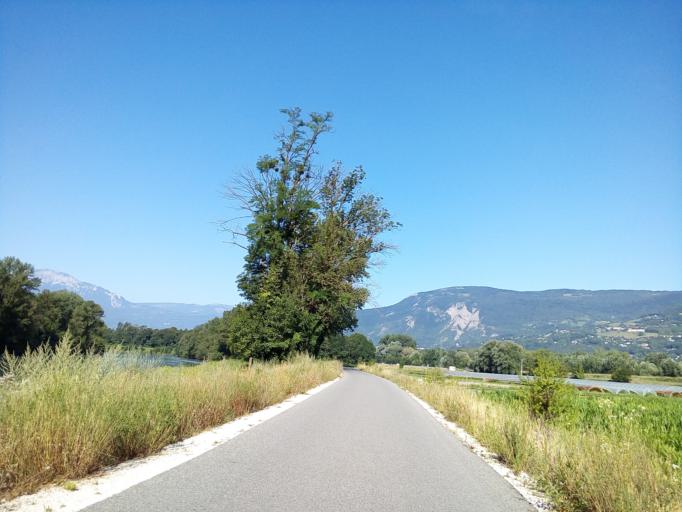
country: FR
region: Rhone-Alpes
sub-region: Departement de l'Isere
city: Montbonnot-Saint-Martin
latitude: 45.2071
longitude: 5.8056
